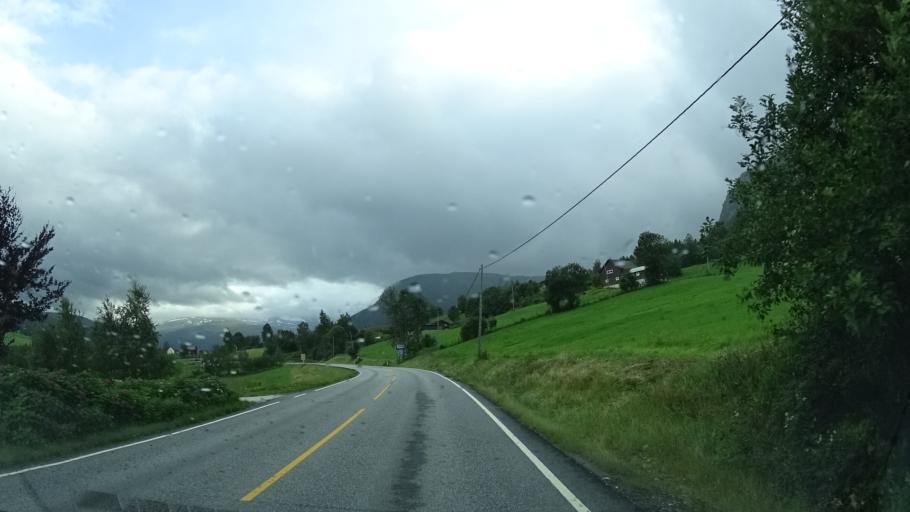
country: NO
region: Hordaland
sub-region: Voss
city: Voss
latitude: 60.6772
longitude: 6.4540
